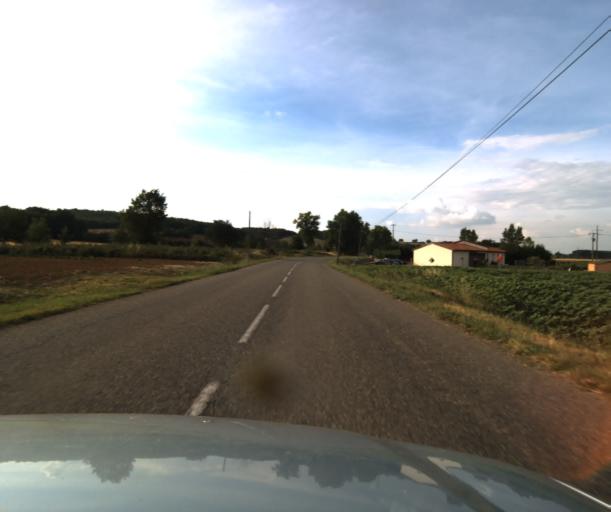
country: FR
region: Midi-Pyrenees
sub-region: Departement du Tarn-et-Garonne
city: Castelsarrasin
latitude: 43.9541
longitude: 1.1027
